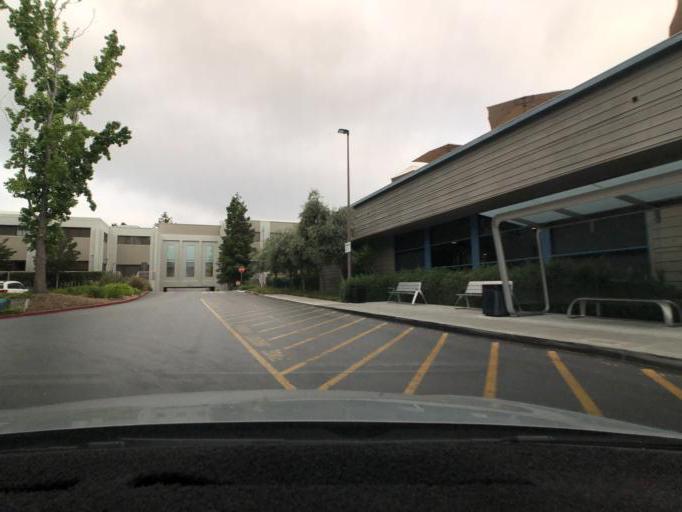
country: US
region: California
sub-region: Santa Clara County
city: Cupertino
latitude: 37.3172
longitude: -122.0512
